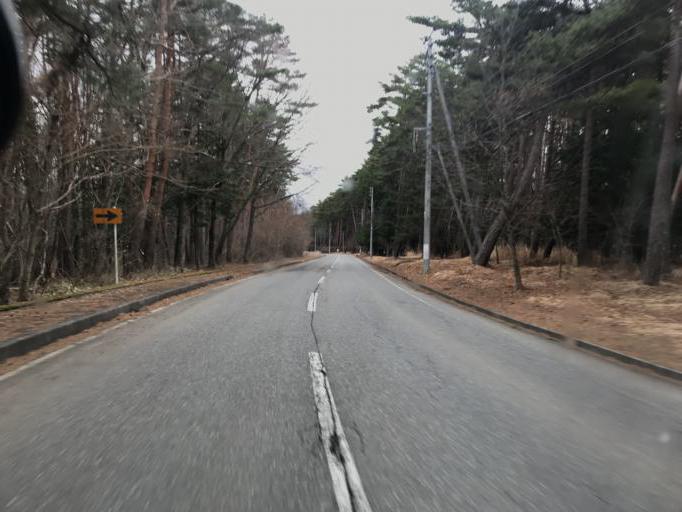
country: JP
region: Nagano
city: Chino
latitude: 35.9215
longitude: 138.2865
